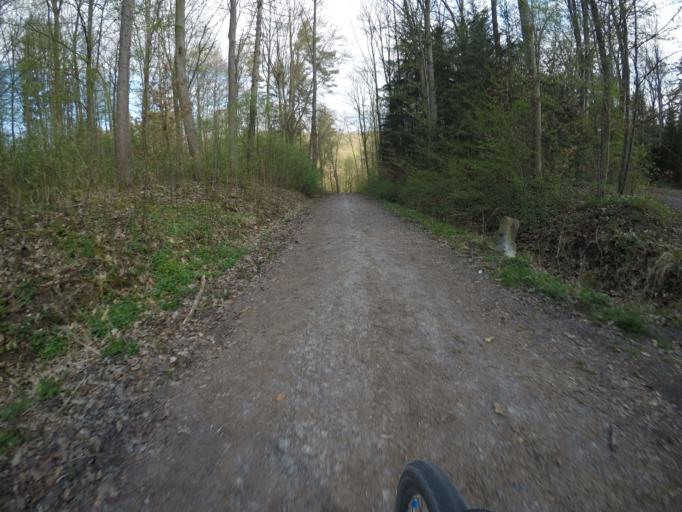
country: DE
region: Baden-Wuerttemberg
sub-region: Regierungsbezirk Stuttgart
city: Gerlingen
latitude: 48.7539
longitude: 9.0831
